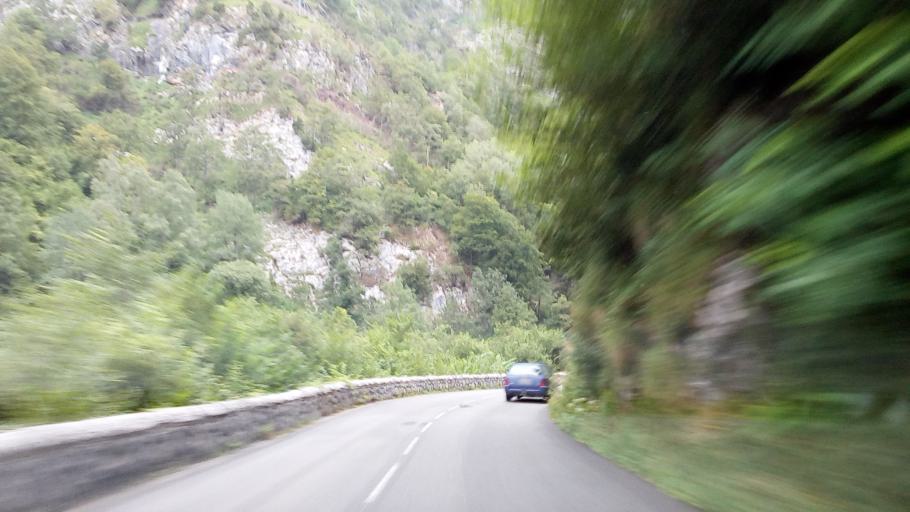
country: FR
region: Aquitaine
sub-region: Departement des Pyrenees-Atlantiques
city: Laruns
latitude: 42.9690
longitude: -0.4380
